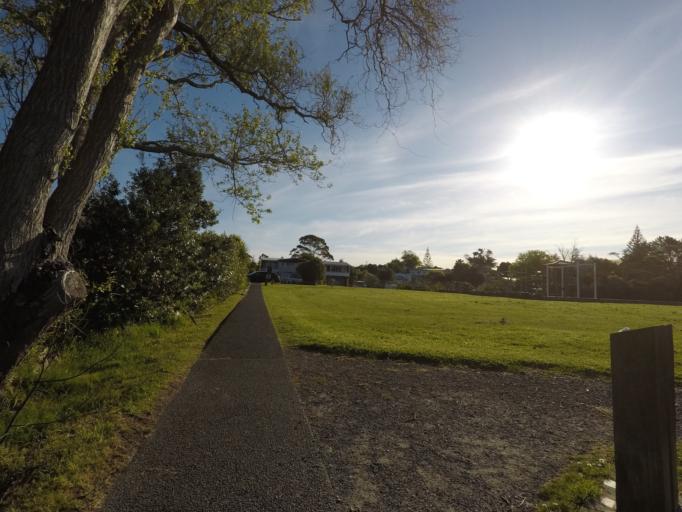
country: NZ
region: Auckland
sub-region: Auckland
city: Rosebank
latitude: -36.8278
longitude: 174.6542
